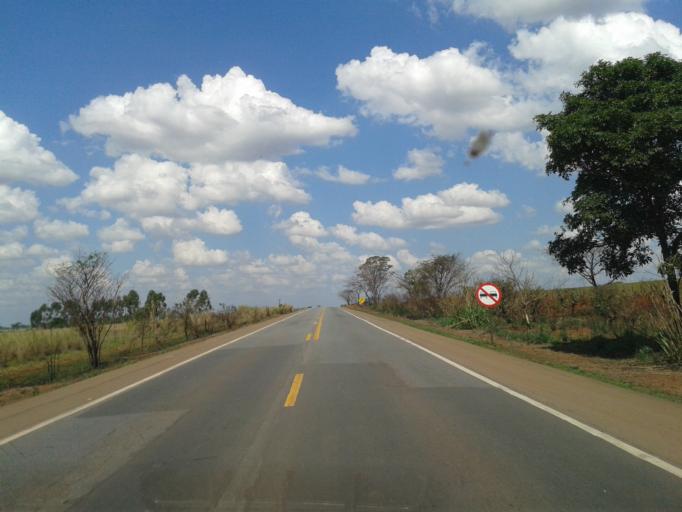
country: BR
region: Minas Gerais
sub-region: Luz
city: Luz
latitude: -19.7633
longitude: -45.7937
